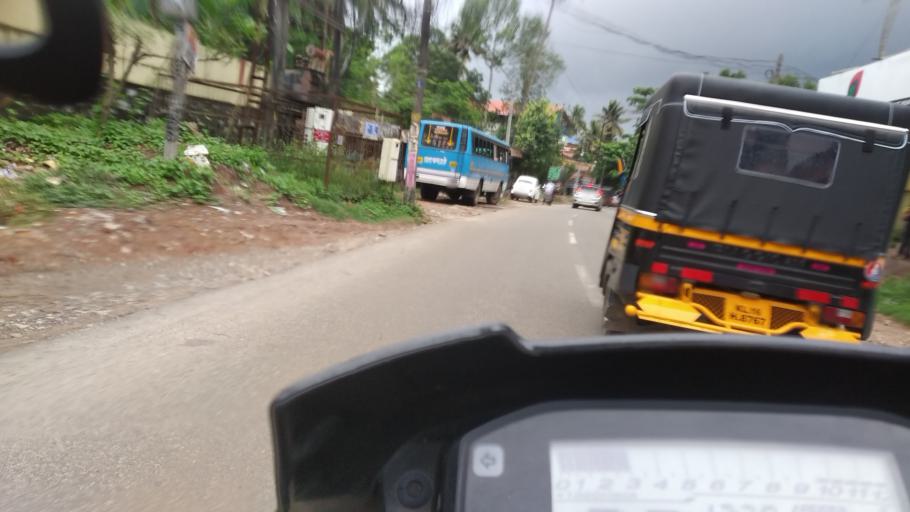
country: IN
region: Kerala
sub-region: Thiruvananthapuram
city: Attingal
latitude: 8.6939
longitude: 76.8120
